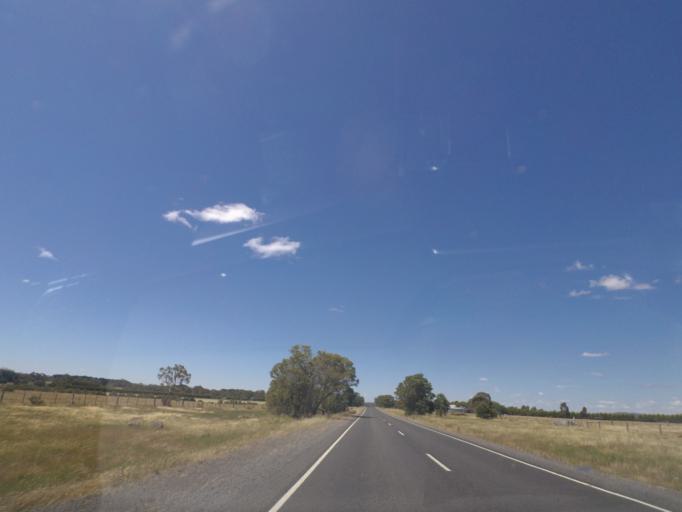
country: AU
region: Victoria
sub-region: Mount Alexander
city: Castlemaine
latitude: -37.2188
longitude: 144.3452
